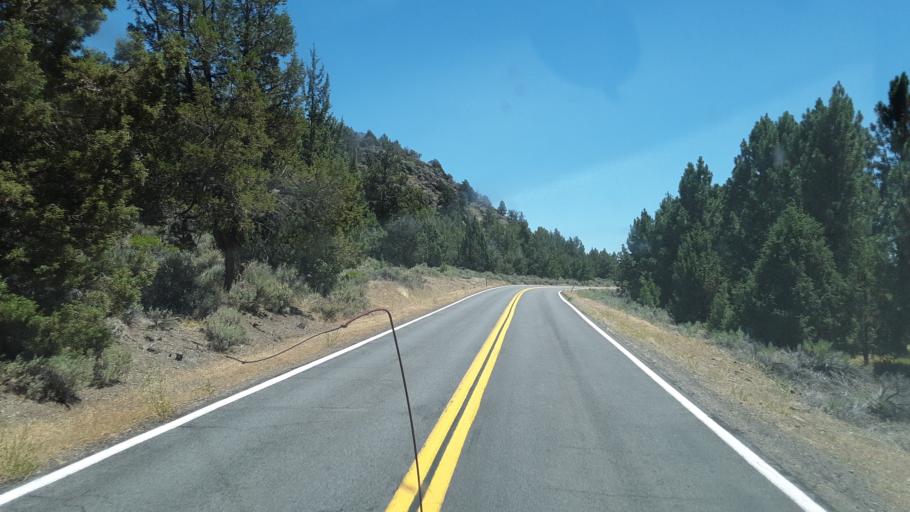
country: US
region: California
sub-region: Lassen County
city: Susanville
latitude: 40.7001
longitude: -120.6715
